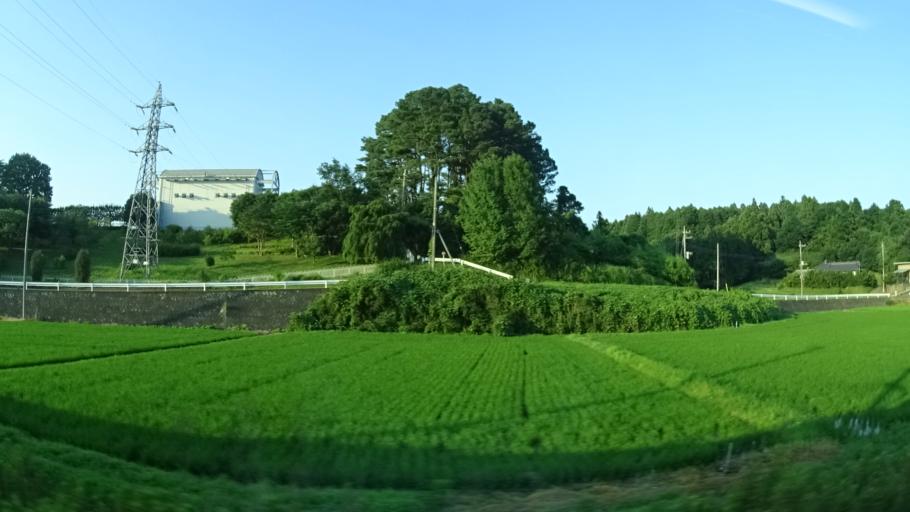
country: JP
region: Ibaraki
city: Ishioka
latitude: 36.1747
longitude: 140.2954
